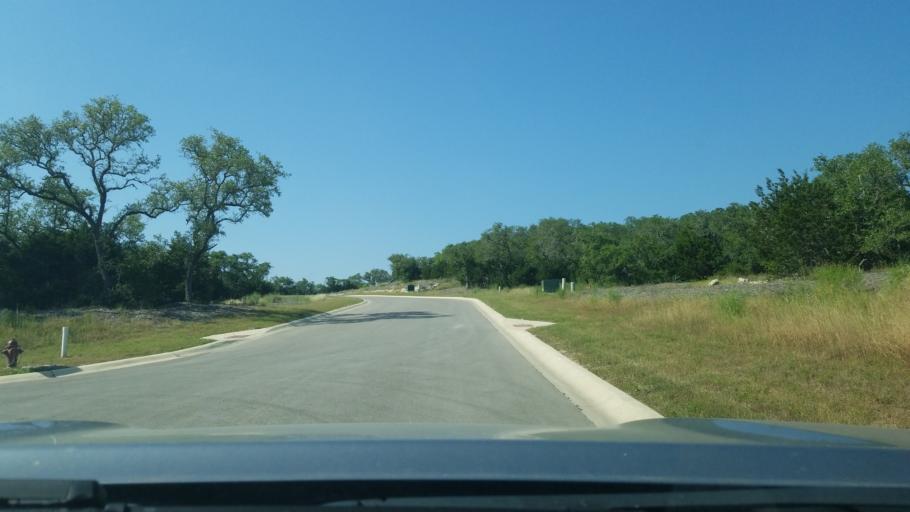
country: US
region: Texas
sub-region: Comal County
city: Bulverde
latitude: 29.7629
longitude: -98.4180
